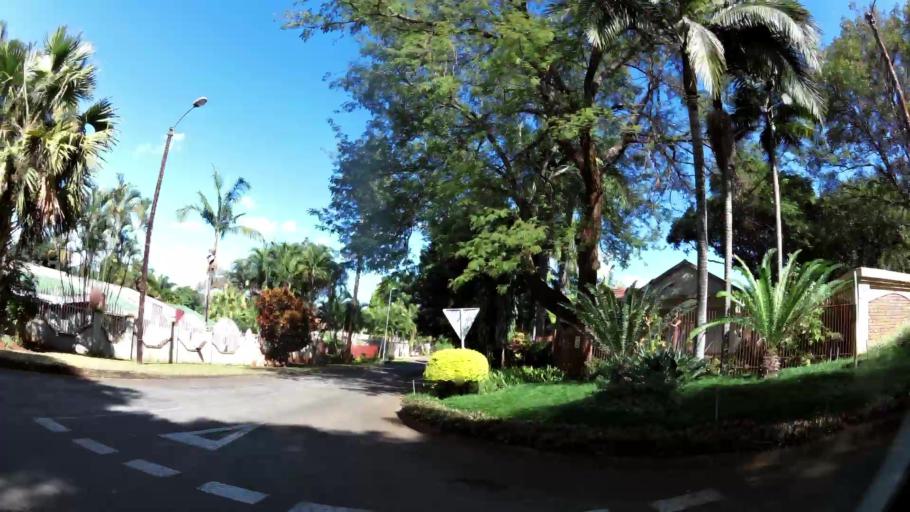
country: ZA
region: Limpopo
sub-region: Mopani District Municipality
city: Tzaneen
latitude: -23.8115
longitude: 30.1566
